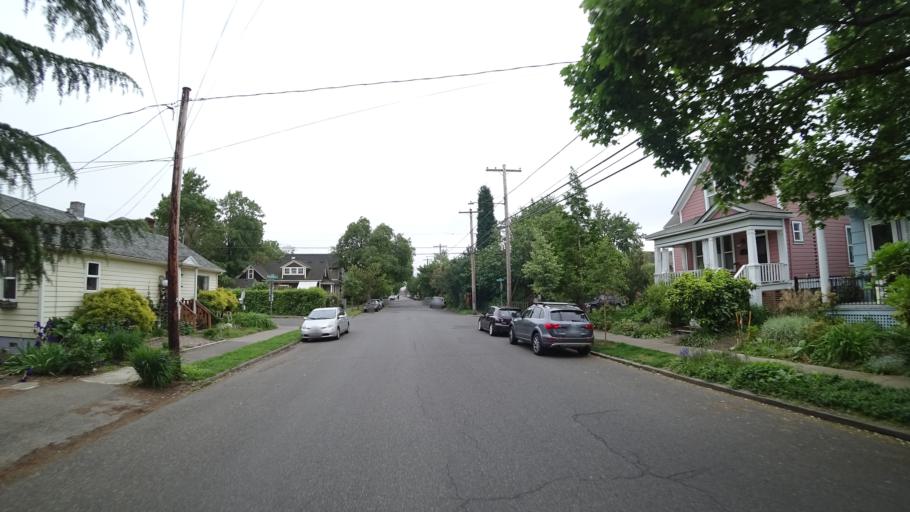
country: US
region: Oregon
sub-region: Multnomah County
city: Portland
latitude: 45.5023
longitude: -122.6446
